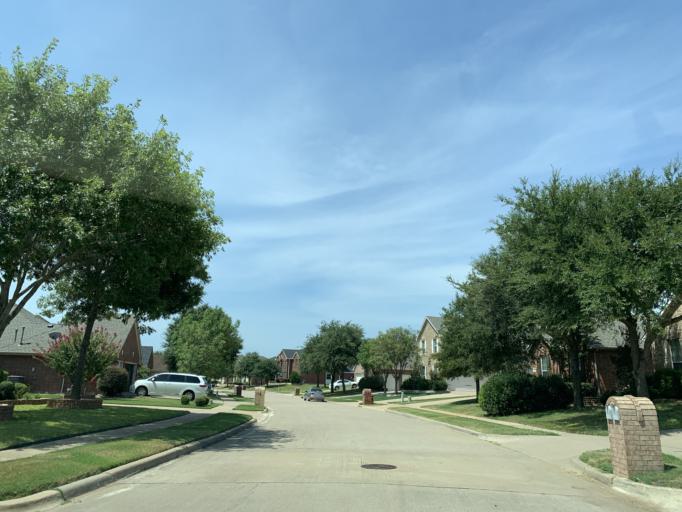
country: US
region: Texas
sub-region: Dallas County
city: Cedar Hill
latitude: 32.6430
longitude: -97.0447
